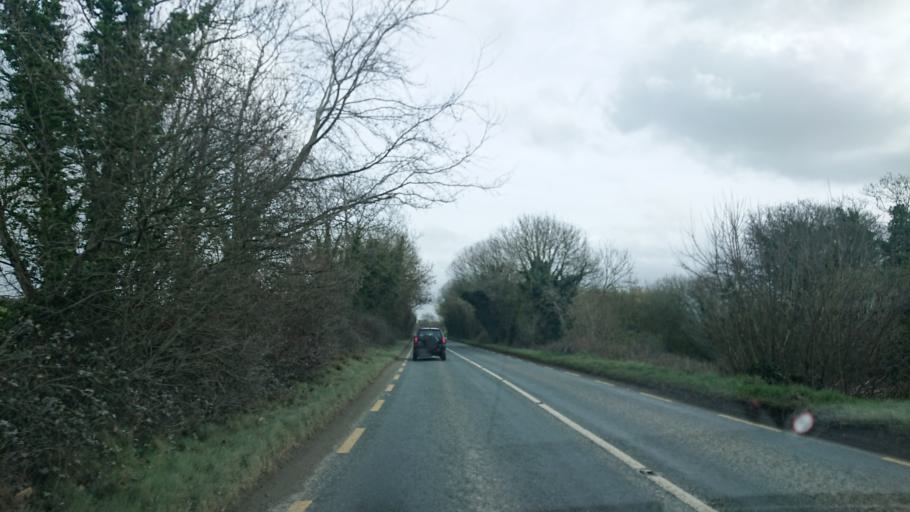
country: IE
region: Leinster
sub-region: Kildare
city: Johnstown
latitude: 53.2030
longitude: -6.6249
